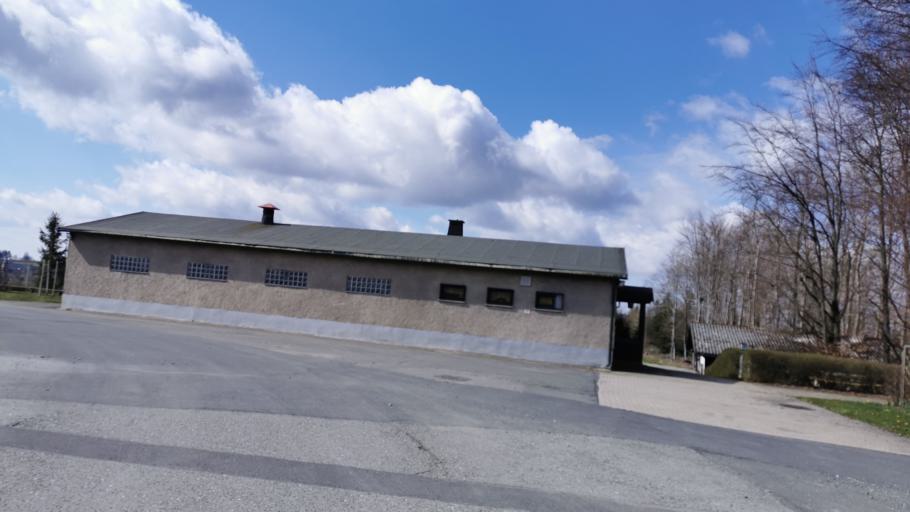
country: DE
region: Bavaria
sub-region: Upper Franconia
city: Teuschnitz
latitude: 50.4210
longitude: 11.3380
